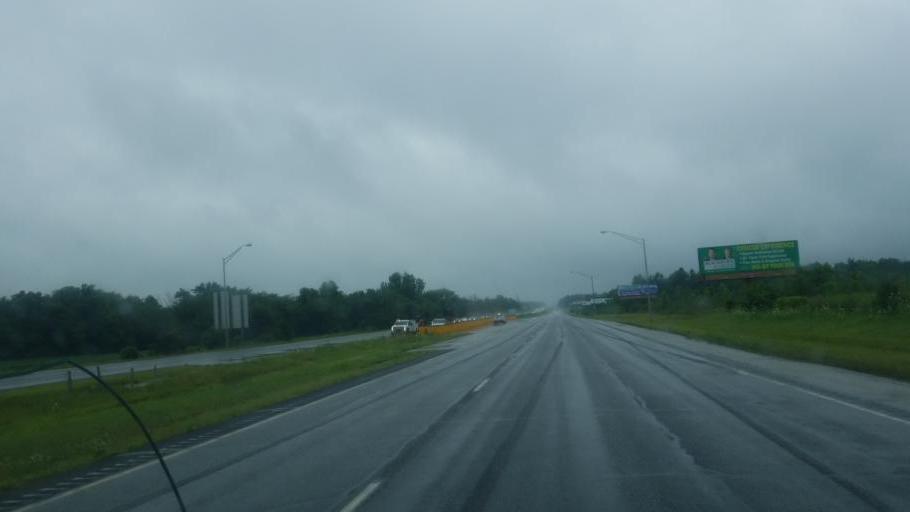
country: US
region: Indiana
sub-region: Grant County
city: Gas City
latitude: 40.5493
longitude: -85.5509
